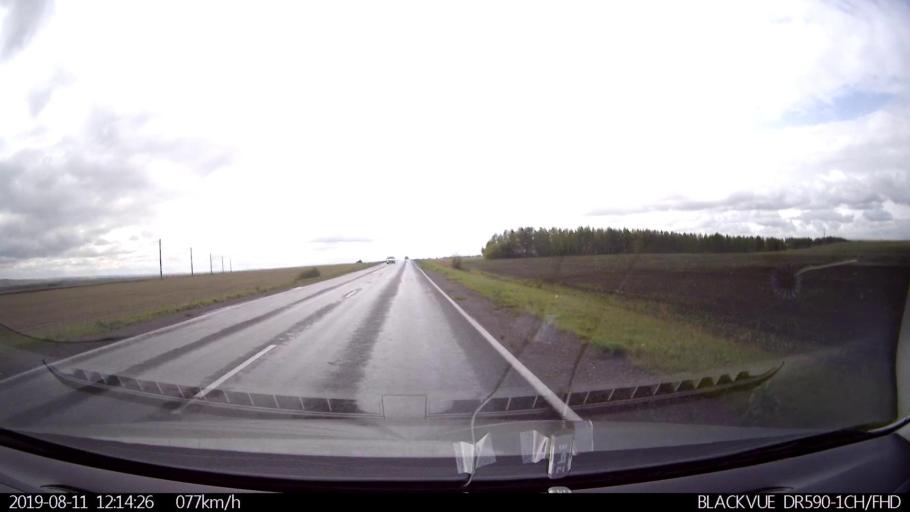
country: RU
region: Ulyanovsk
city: Ignatovka
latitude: 53.9523
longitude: 47.9802
